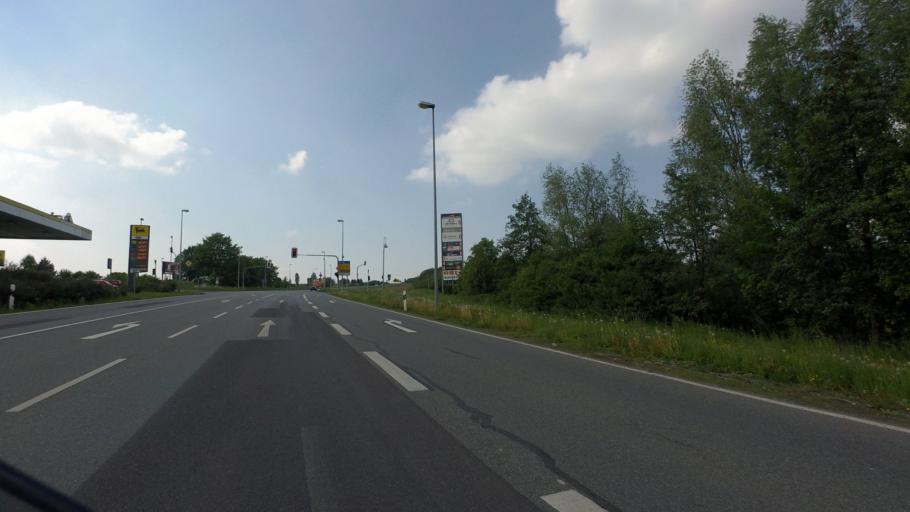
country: DE
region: Saxony
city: Lobau
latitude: 51.1056
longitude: 14.6545
